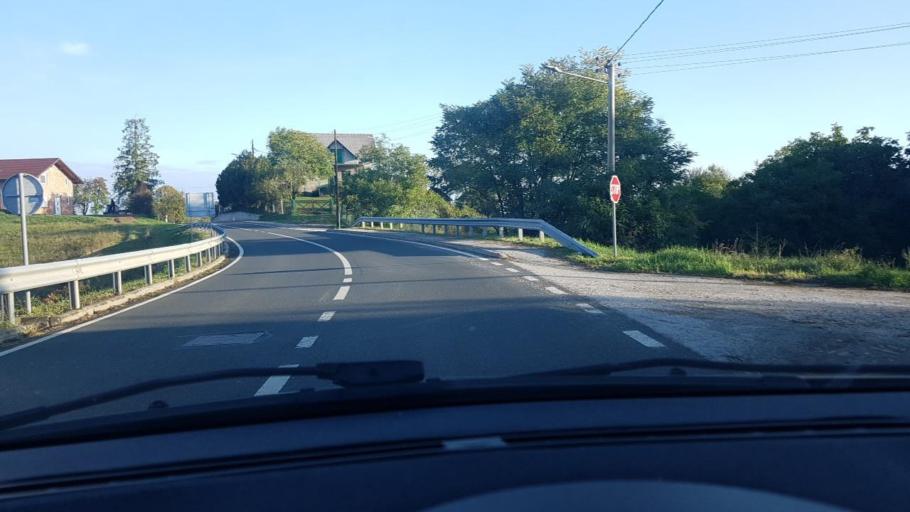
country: HR
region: Krapinsko-Zagorska
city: Marija Bistrica
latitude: 45.9620
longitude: 16.0923
